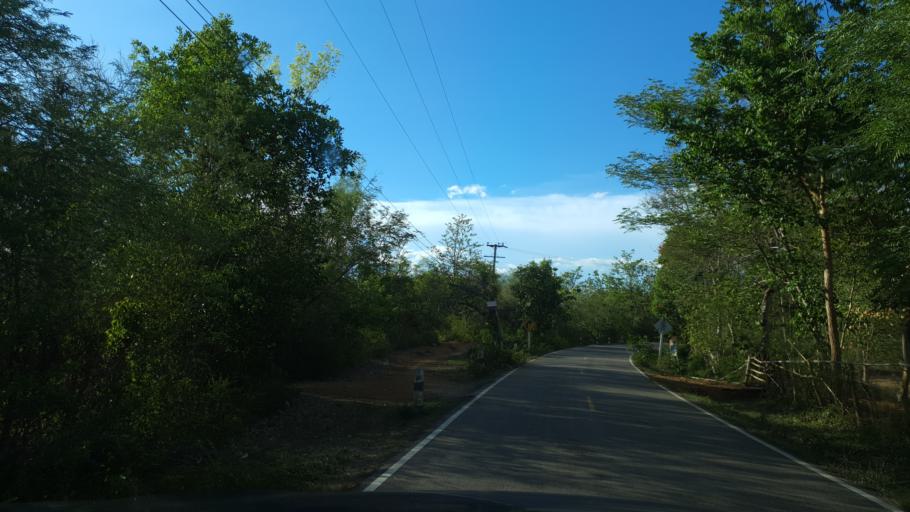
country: TH
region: Lampang
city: Sop Prap
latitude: 17.8771
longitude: 99.3089
